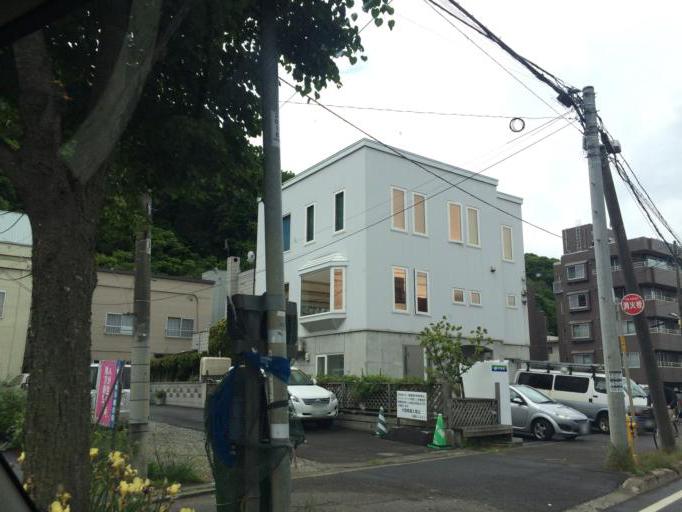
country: JP
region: Hokkaido
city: Sapporo
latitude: 43.0261
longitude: 141.3399
